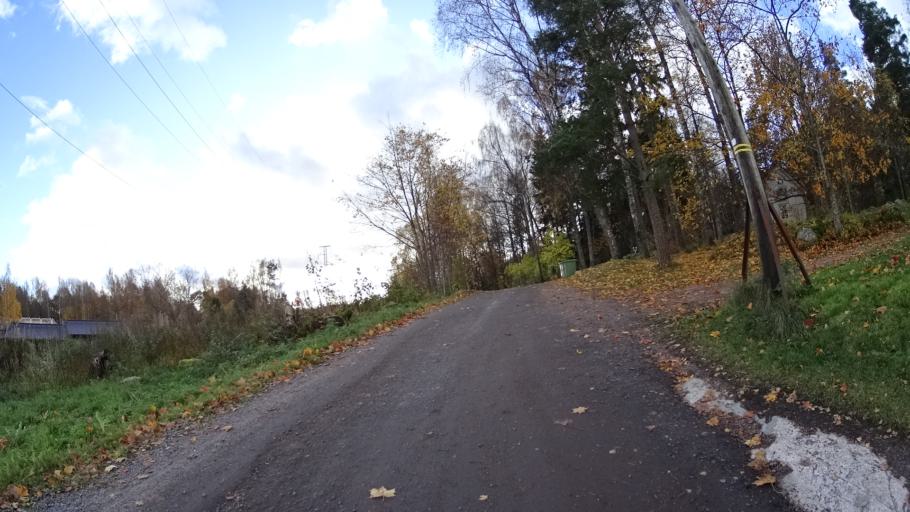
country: FI
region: Uusimaa
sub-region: Helsinki
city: Kilo
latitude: 60.2649
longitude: 24.7941
